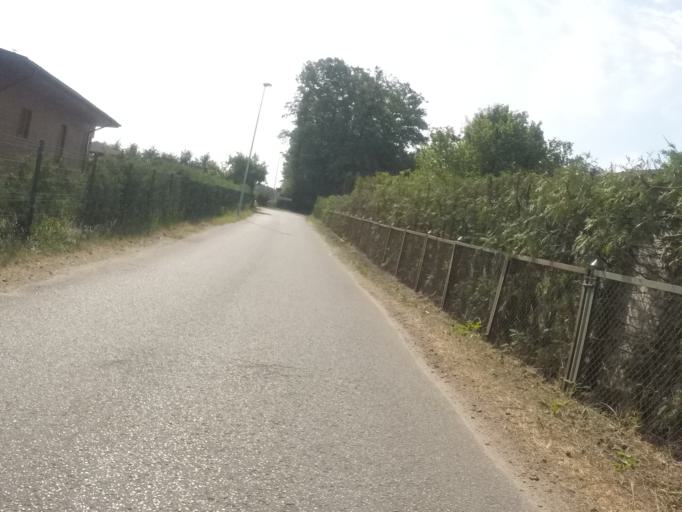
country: LT
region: Alytaus apskritis
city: Druskininkai
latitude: 54.0310
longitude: 24.0745
